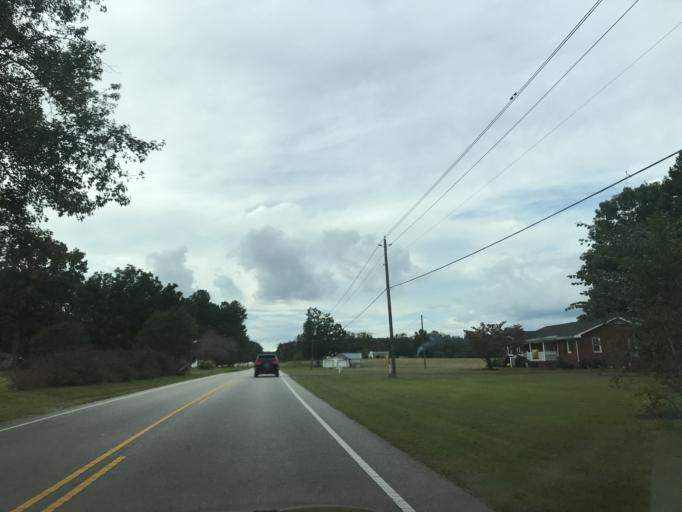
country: US
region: North Carolina
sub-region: Franklin County
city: Youngsville
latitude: 36.0055
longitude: -78.4337
